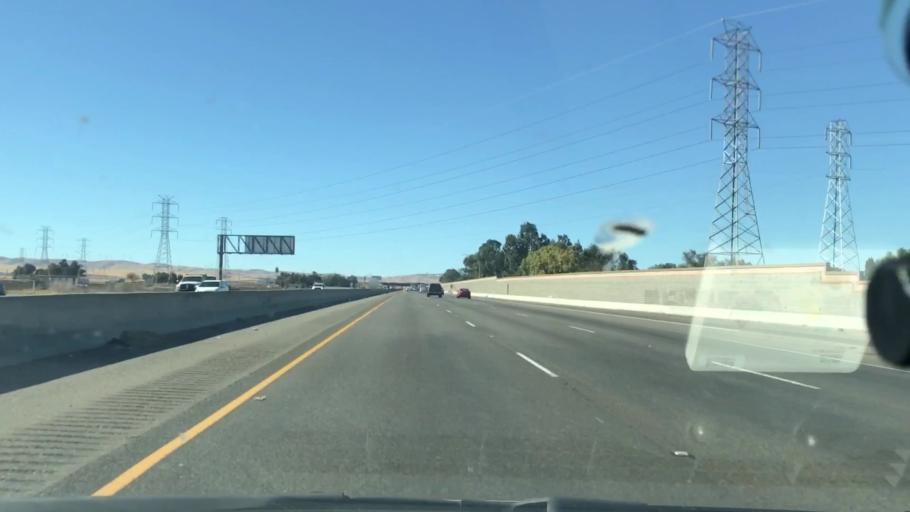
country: US
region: California
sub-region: San Joaquin County
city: Mountain House
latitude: 37.7406
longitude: -121.5028
